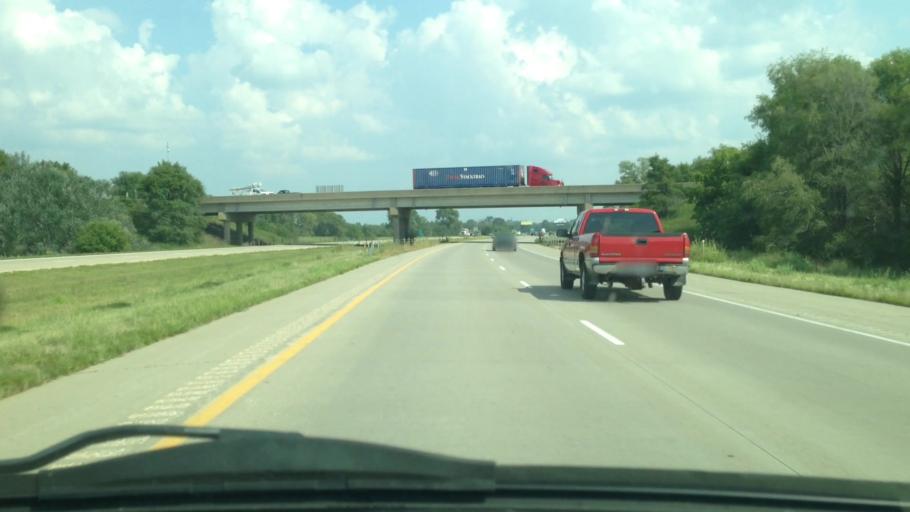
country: US
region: Iowa
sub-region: Black Hawk County
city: Elk Run Heights
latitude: 42.4583
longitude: -92.2559
